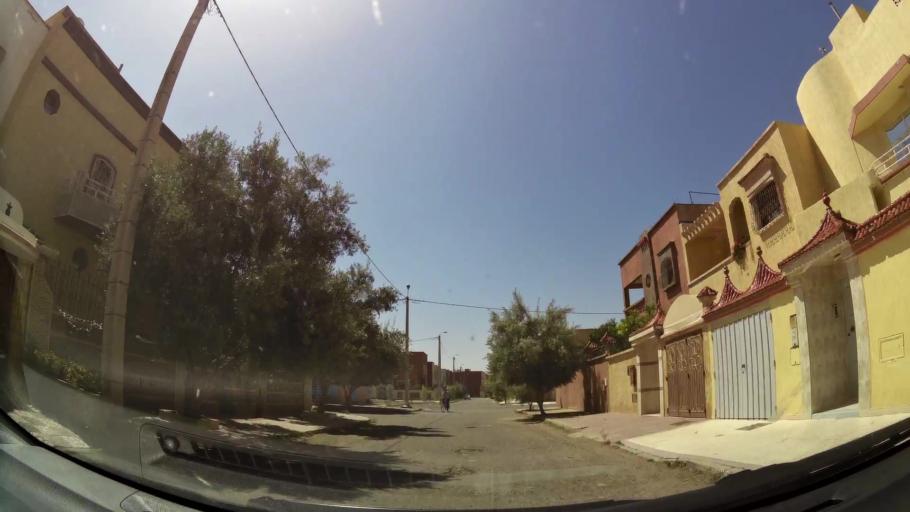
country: MA
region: Souss-Massa-Draa
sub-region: Inezgane-Ait Mellou
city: Inezgane
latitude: 30.3228
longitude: -9.5055
